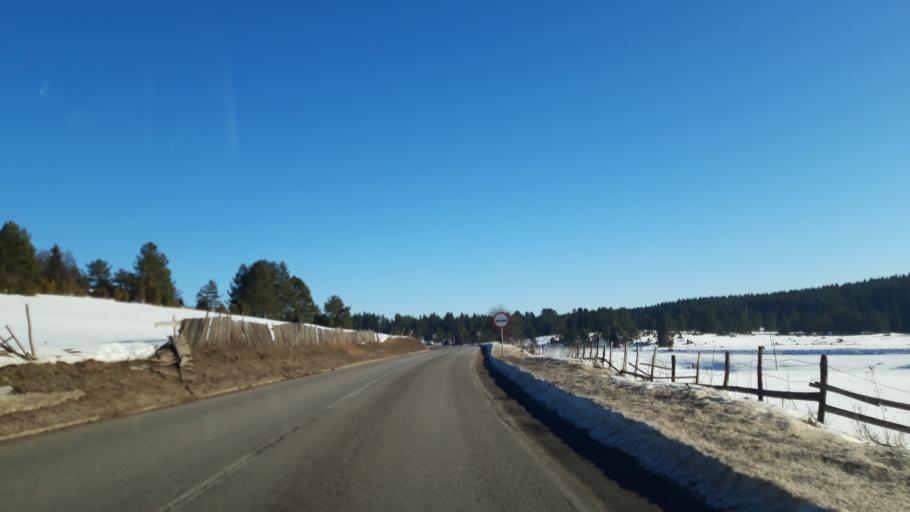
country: BA
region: Republika Srpska
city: Sokolac
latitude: 43.9207
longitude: 18.6848
